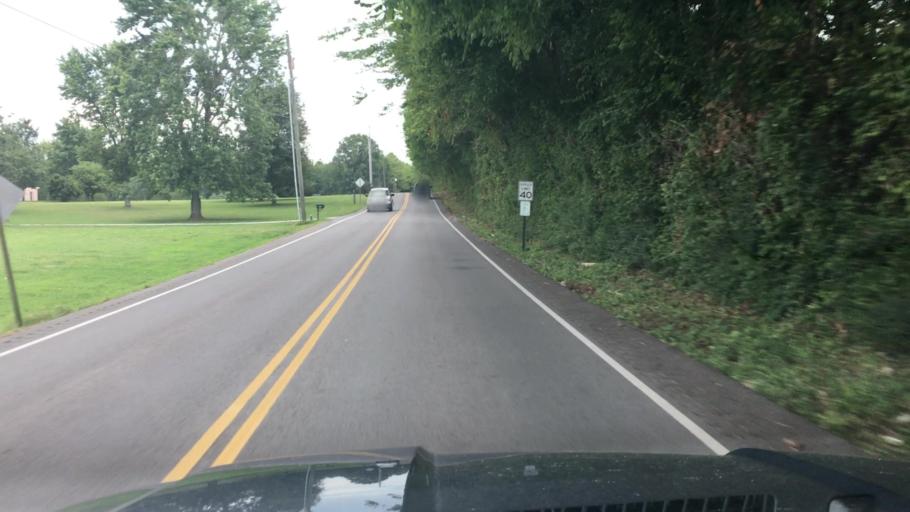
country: US
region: Tennessee
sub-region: Williamson County
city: Thompson's Station
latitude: 35.8079
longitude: -86.8623
